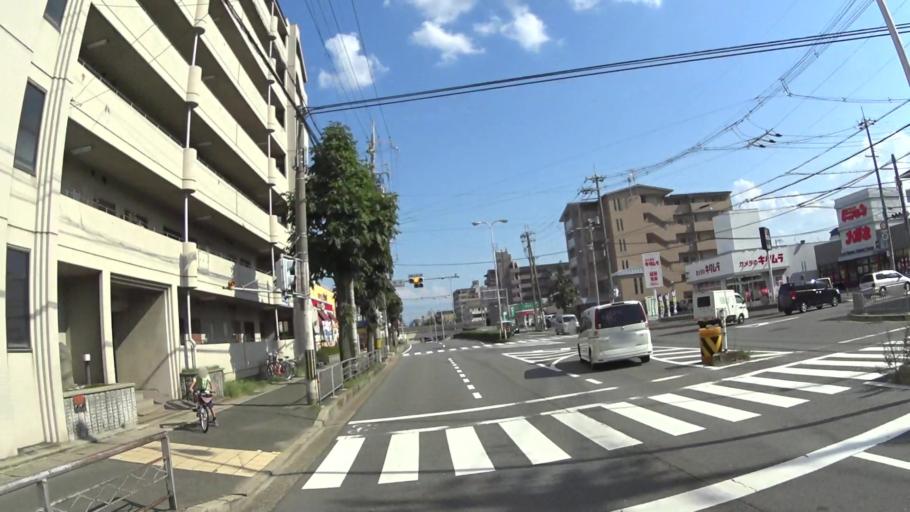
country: JP
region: Kyoto
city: Muko
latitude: 34.9747
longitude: 135.7143
